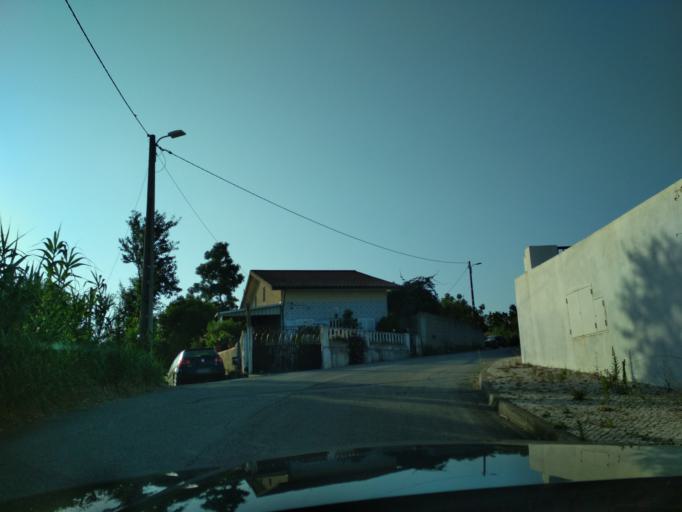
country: PT
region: Coimbra
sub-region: Coimbra
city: Coimbra
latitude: 40.2670
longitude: -8.4532
